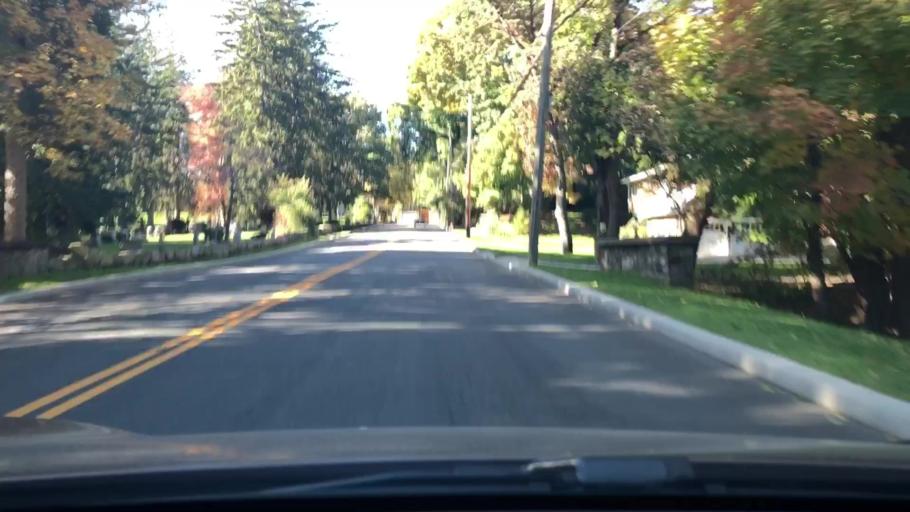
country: US
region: New York
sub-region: Westchester County
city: Rye
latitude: 40.9801
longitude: -73.7003
